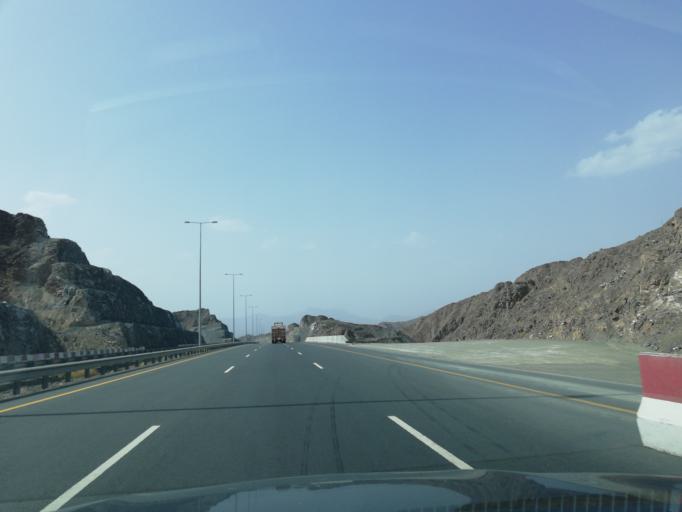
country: OM
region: Muhafazat ad Dakhiliyah
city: Sufalat Sama'il
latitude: 22.9948
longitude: 58.2313
